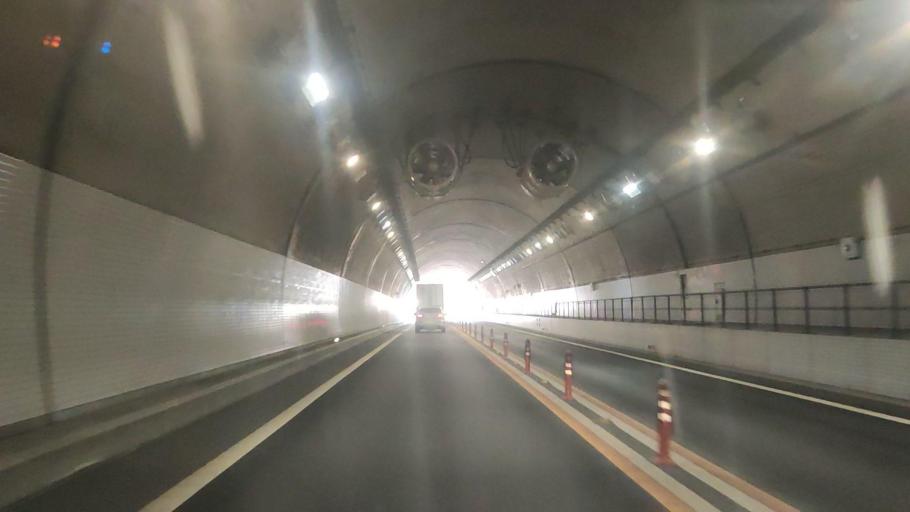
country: JP
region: Fukuoka
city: Kanda
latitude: 33.7680
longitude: 130.9653
